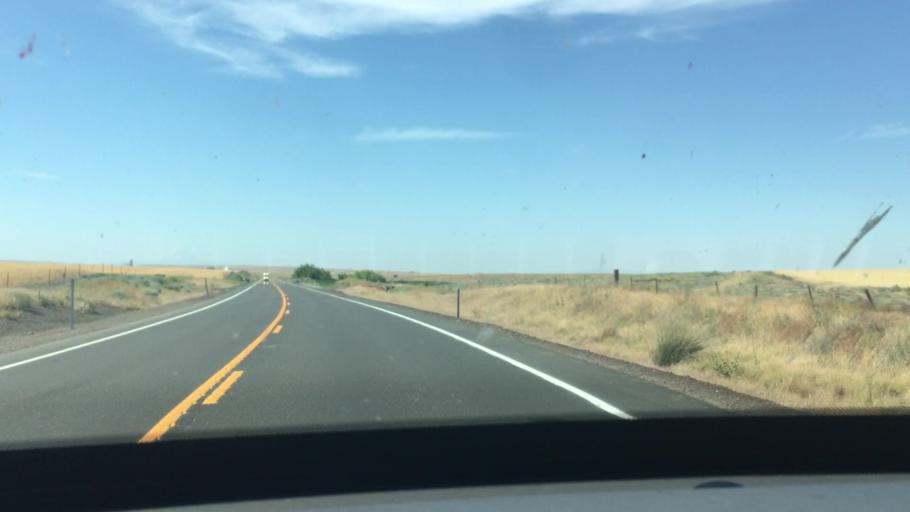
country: US
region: Oregon
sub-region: Sherman County
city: Moro
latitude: 45.3321
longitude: -120.7692
